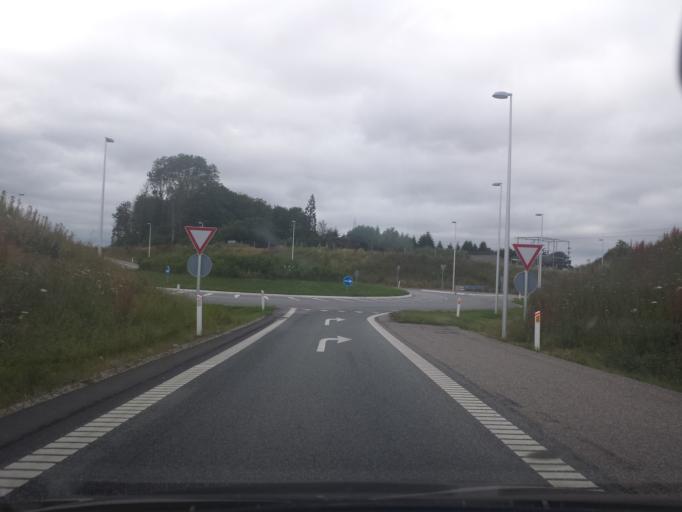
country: DK
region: South Denmark
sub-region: Sonderborg Kommune
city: Grasten
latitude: 54.9524
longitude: 9.6385
